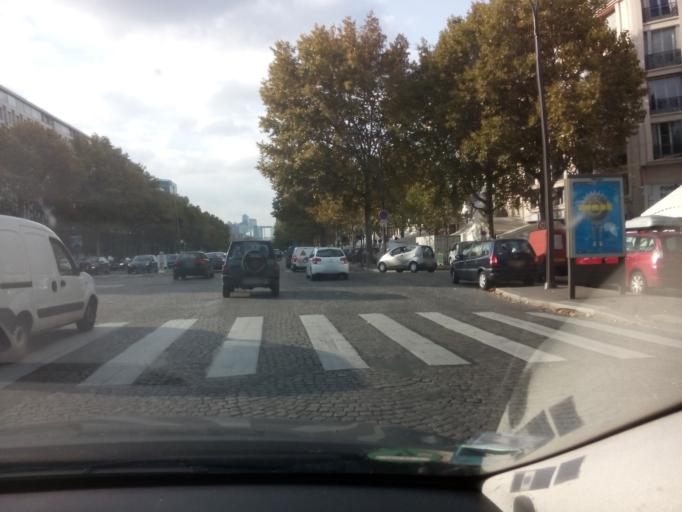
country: FR
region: Ile-de-France
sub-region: Departement des Hauts-de-Seine
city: Levallois-Perret
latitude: 48.8762
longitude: 2.2876
